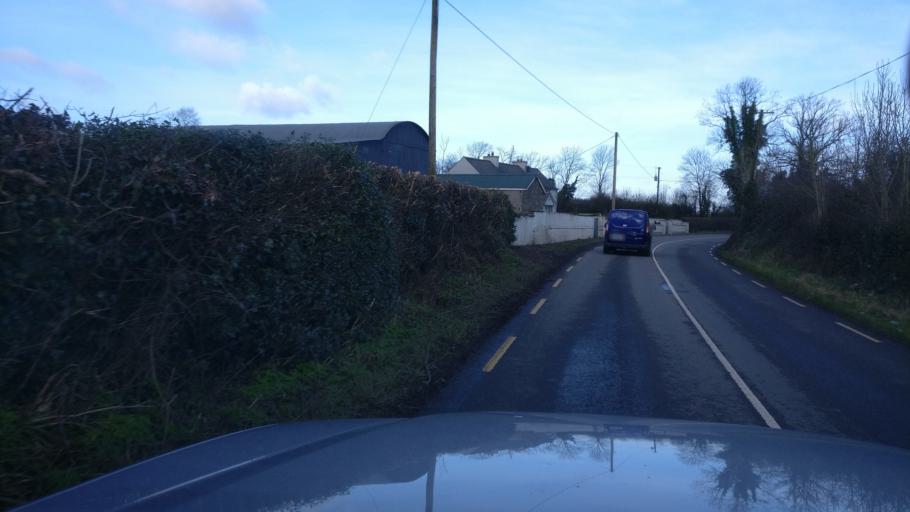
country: IE
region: Leinster
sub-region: Kilkenny
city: Castlecomer
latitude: 52.8425
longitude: -7.1853
